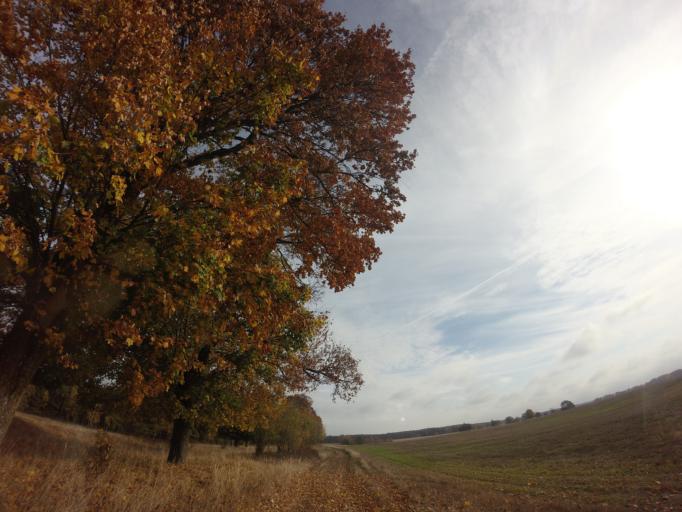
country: PL
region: West Pomeranian Voivodeship
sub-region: Powiat choszczenski
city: Recz
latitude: 53.2602
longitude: 15.6456
